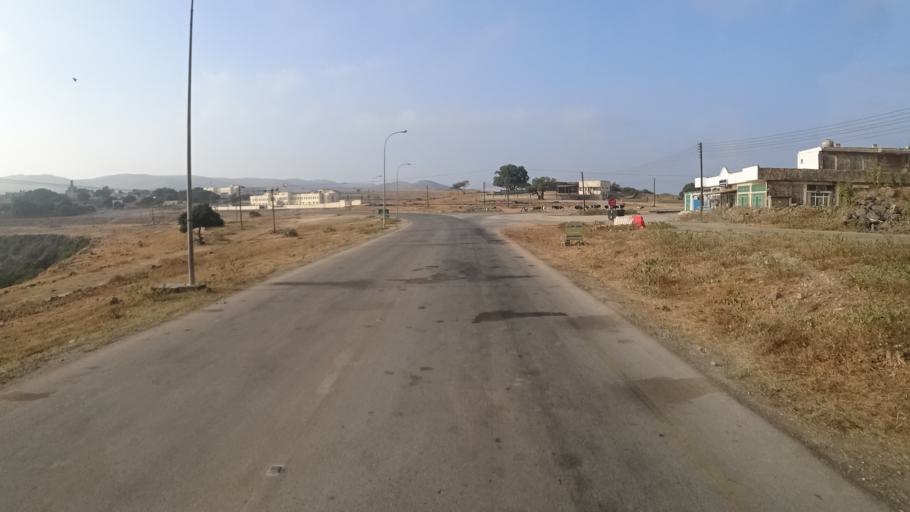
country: OM
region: Zufar
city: Salalah
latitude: 17.1239
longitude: 53.9991
